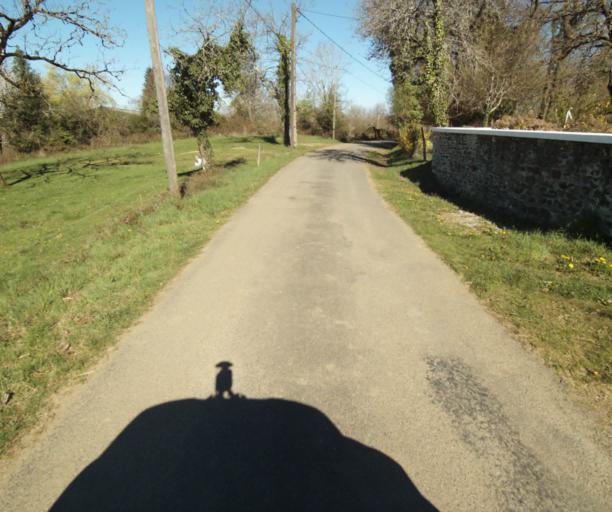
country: FR
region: Limousin
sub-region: Departement de la Correze
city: Chamboulive
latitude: 45.4069
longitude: 1.7301
